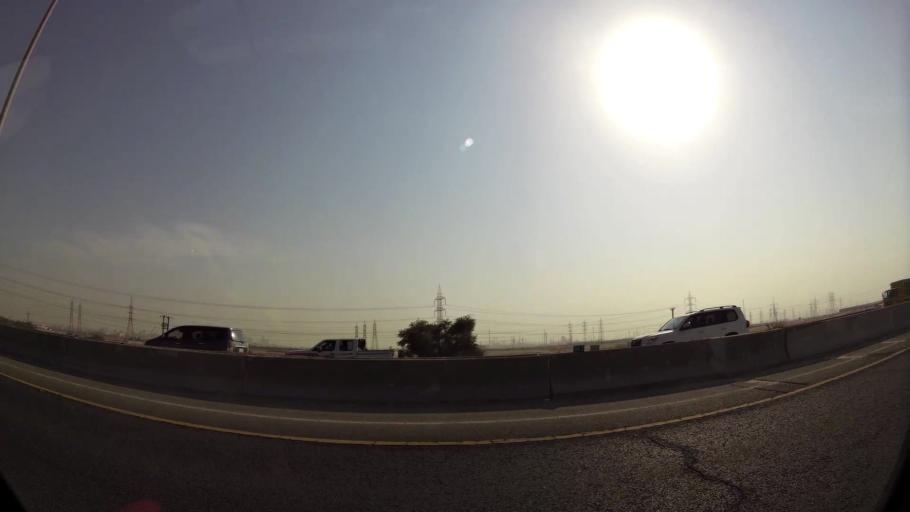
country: KW
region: Al Ahmadi
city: Al Ahmadi
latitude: 29.0681
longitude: 48.0990
